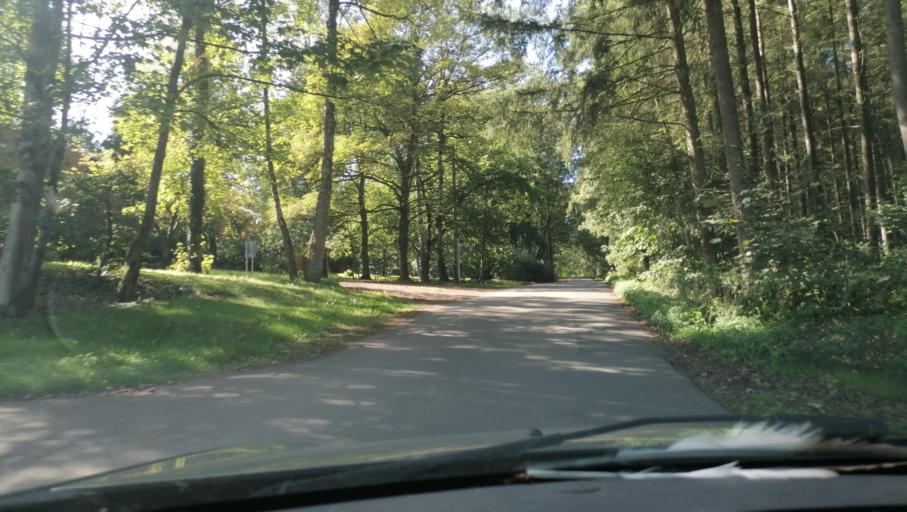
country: BE
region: Wallonia
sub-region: Province de Namur
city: Profondeville
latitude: 50.3550
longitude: 4.8634
